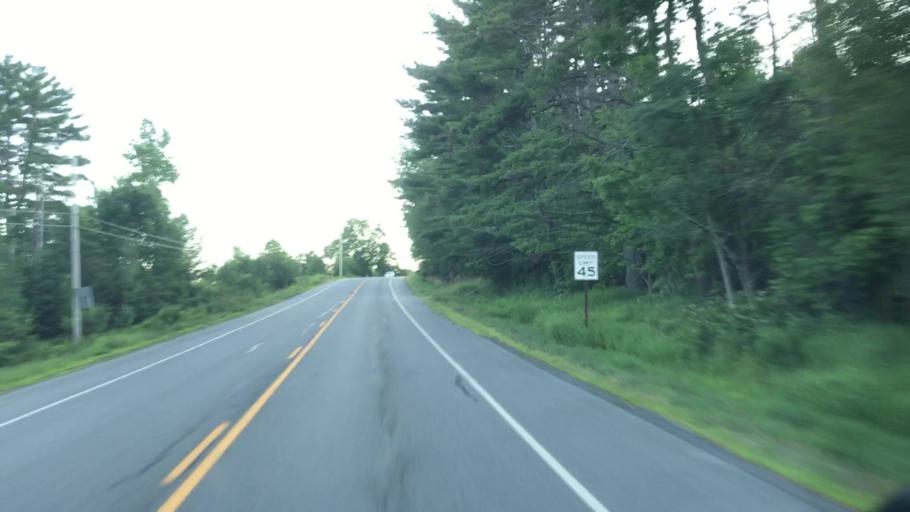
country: US
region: Maine
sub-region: Penobscot County
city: Lincoln
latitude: 45.3755
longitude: -68.4661
